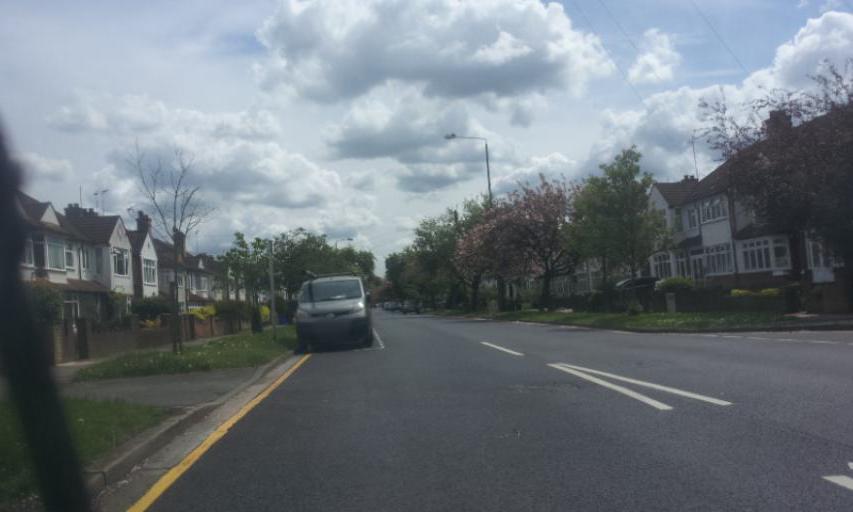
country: GB
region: England
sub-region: Greater London
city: Bromley
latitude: 51.4016
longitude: 0.0069
